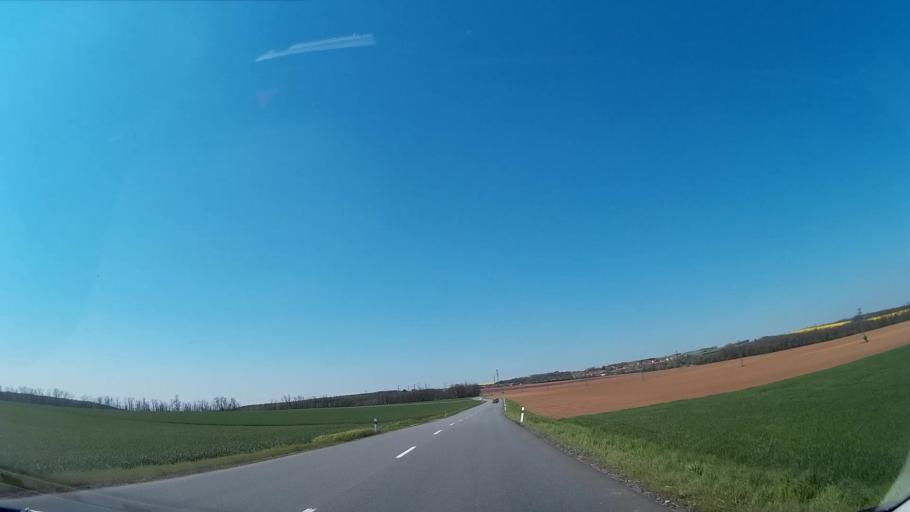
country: CZ
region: South Moravian
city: Moravsky Krumlov
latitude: 49.0736
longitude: 16.3241
